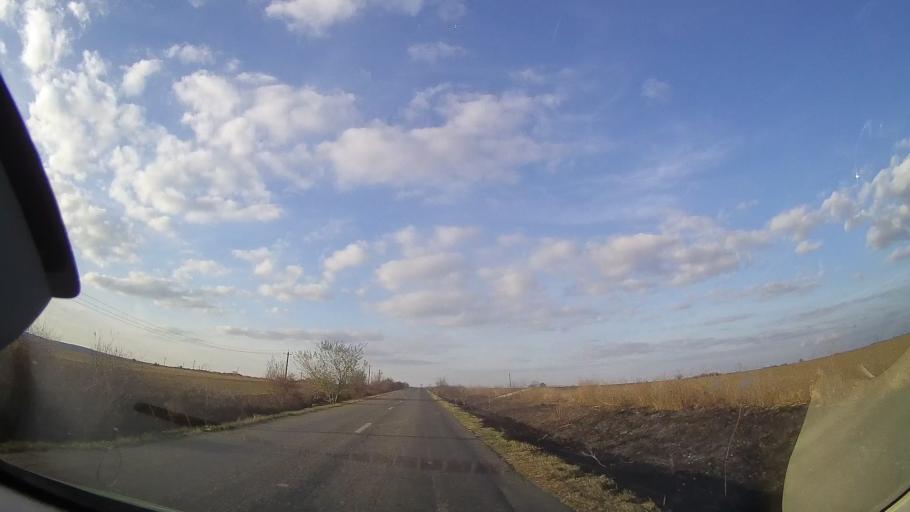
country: RO
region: Constanta
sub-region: Comuna Dumbraveni
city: Dumbraveni
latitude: 43.9316
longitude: 28.0268
